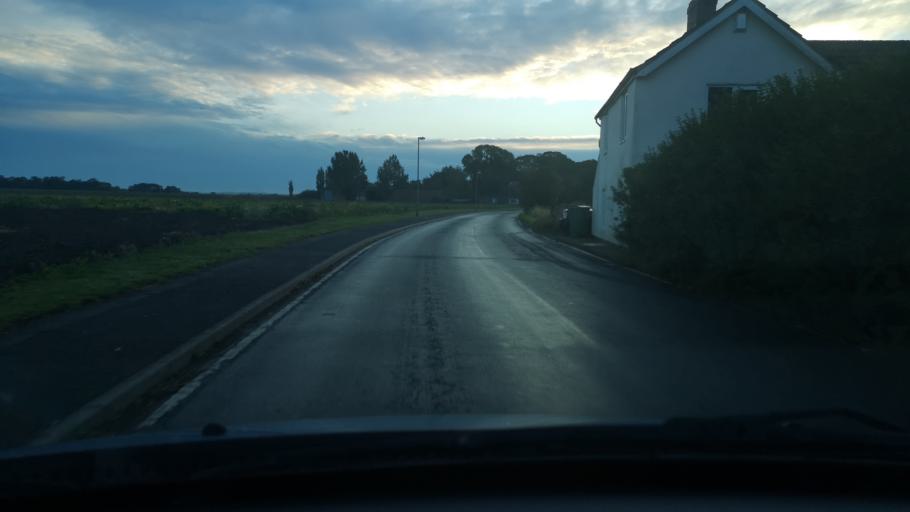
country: GB
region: England
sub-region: East Riding of Yorkshire
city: Laxton
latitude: 53.6998
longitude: -0.8062
